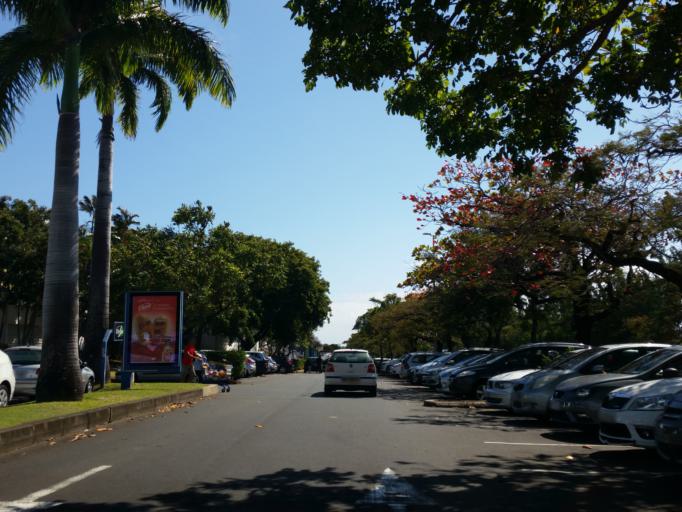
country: RE
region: Reunion
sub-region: Reunion
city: Sainte-Marie
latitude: -20.8919
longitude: 55.5012
